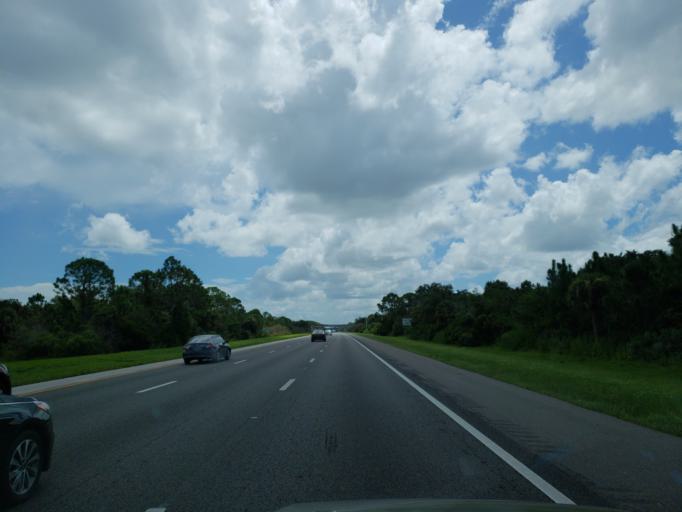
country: US
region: Florida
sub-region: Sarasota County
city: Nokomis
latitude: 27.1269
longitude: -82.4015
